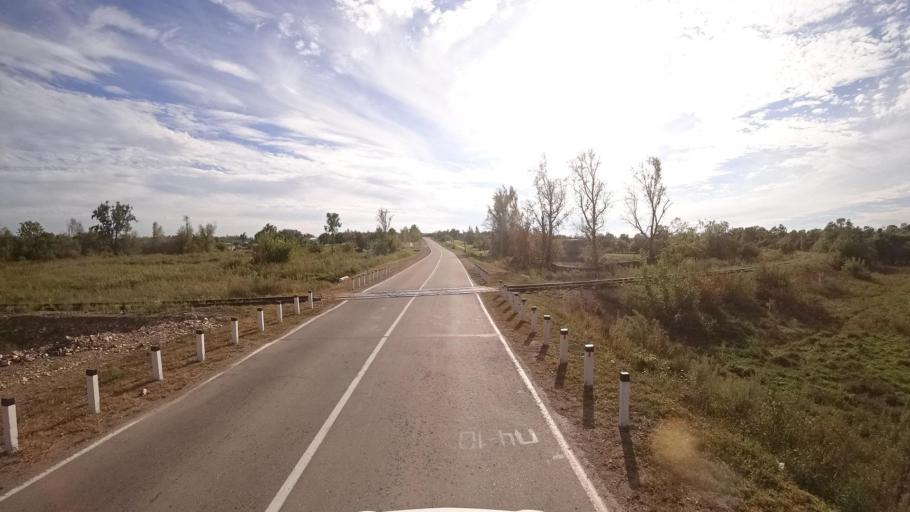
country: RU
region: Primorskiy
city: Dostoyevka
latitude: 44.3105
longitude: 133.4558
